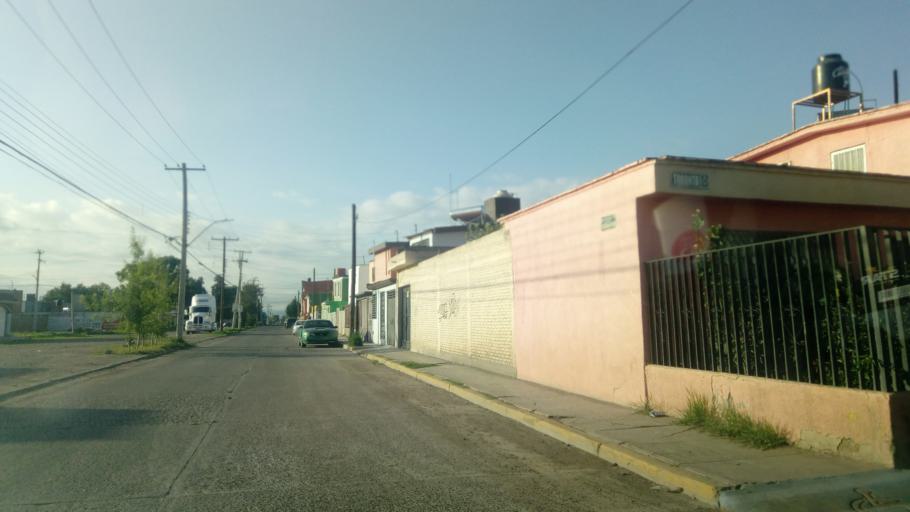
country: MX
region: Durango
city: Victoria de Durango
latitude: 24.0500
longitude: -104.6177
